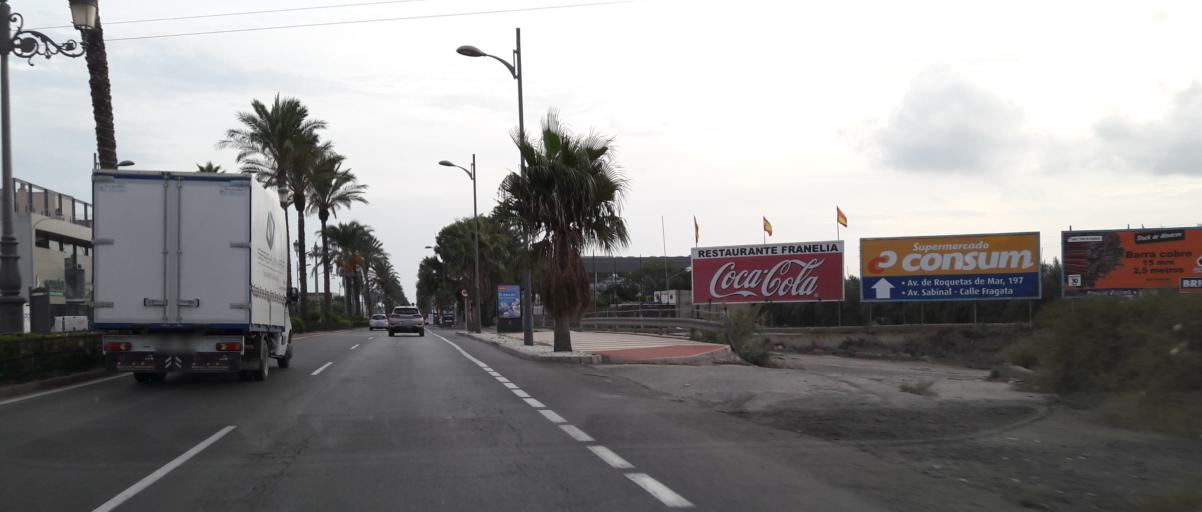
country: ES
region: Andalusia
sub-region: Provincia de Almeria
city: Roquetas de Mar
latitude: 36.7835
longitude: -2.6079
